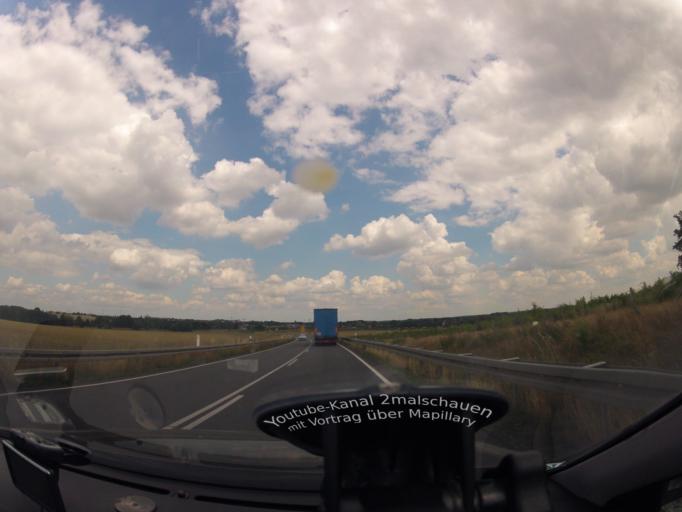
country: DE
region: Saxony
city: Eilenburg
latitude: 51.4364
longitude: 12.6045
